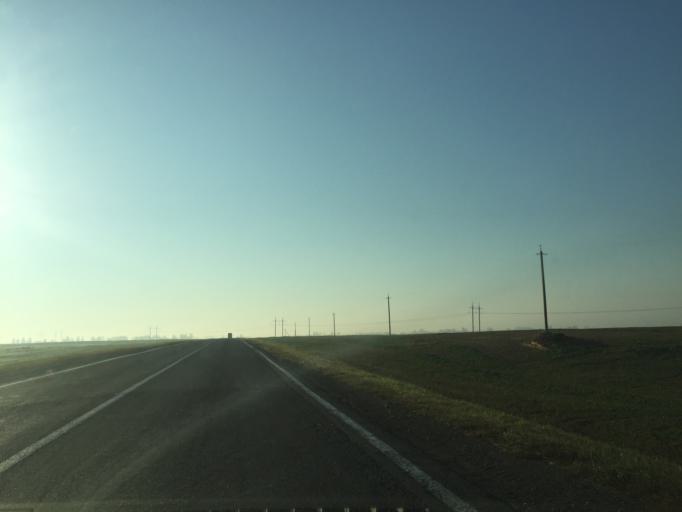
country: BY
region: Gomel
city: Buda-Kashalyova
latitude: 52.8303
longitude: 30.7134
